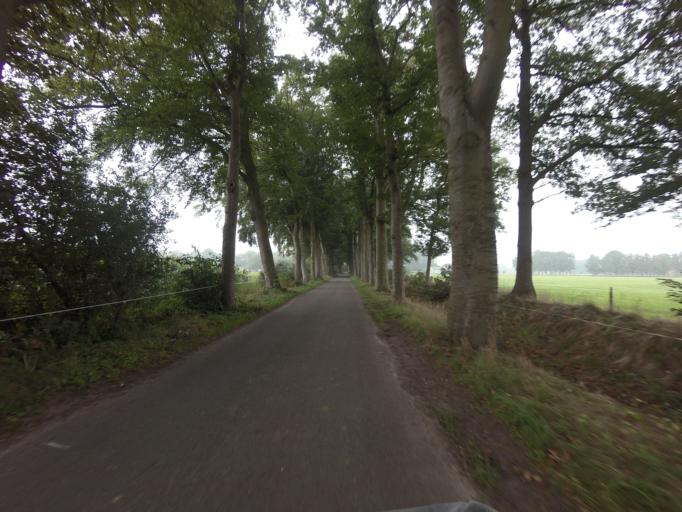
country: NL
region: Overijssel
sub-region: Gemeente Deventer
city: Schalkhaar
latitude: 52.2750
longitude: 6.2465
